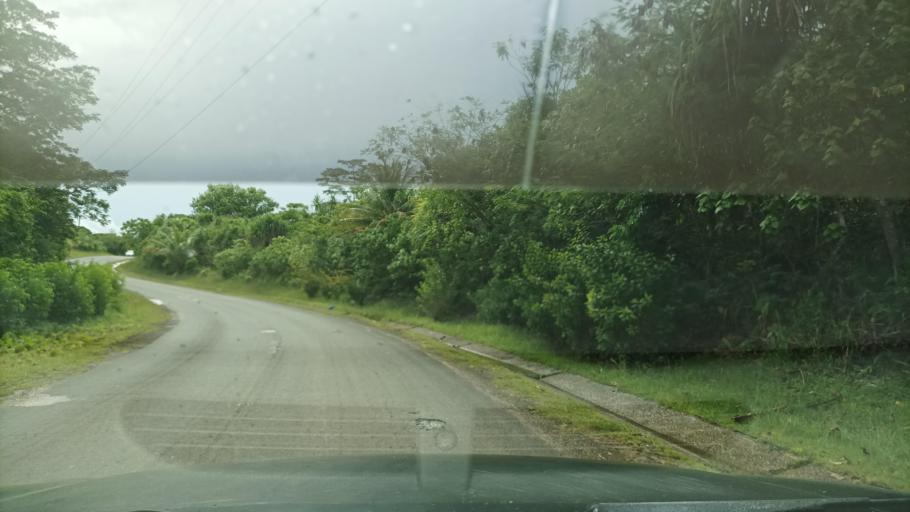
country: FM
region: Yap
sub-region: Weloy Municipality
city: Colonia
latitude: 9.5481
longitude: 138.1578
